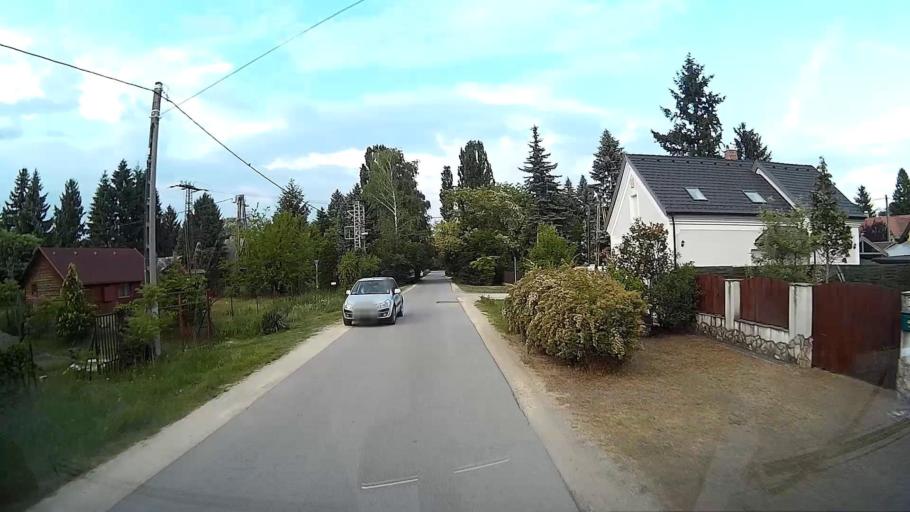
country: HU
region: Pest
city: God
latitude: 47.6739
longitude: 19.1137
